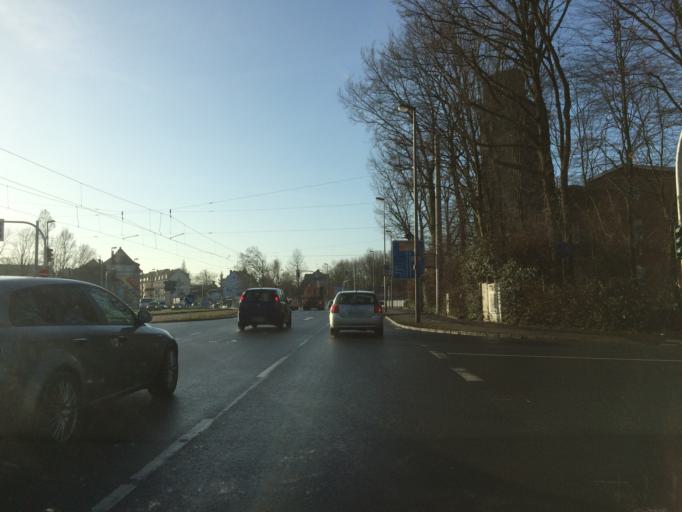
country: DE
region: North Rhine-Westphalia
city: Bochum-Hordel
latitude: 51.4970
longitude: 7.1889
